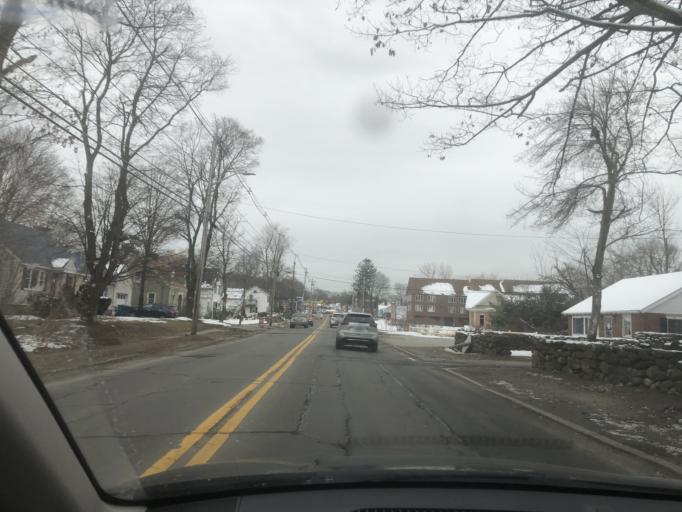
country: US
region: Massachusetts
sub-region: Middlesex County
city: Tewksbury
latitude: 42.6082
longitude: -71.2283
